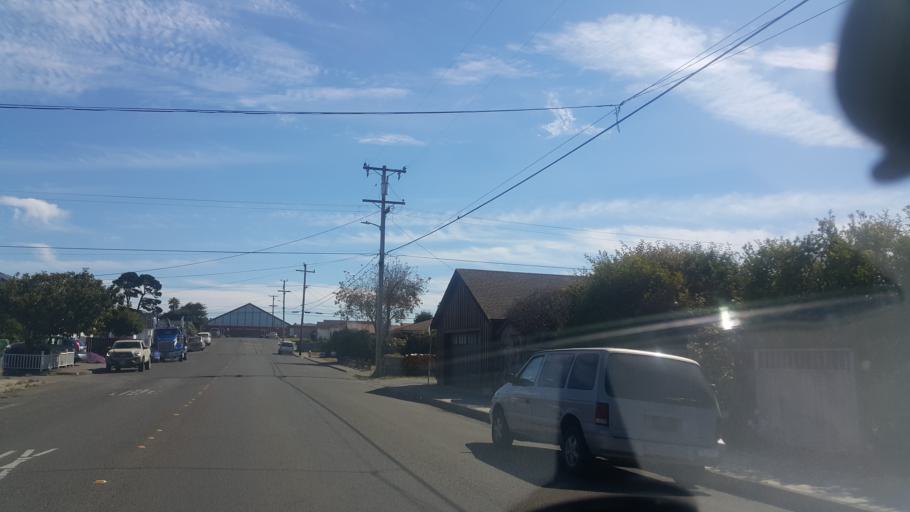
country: US
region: California
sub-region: Mendocino County
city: Fort Bragg
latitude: 39.4391
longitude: -123.7978
